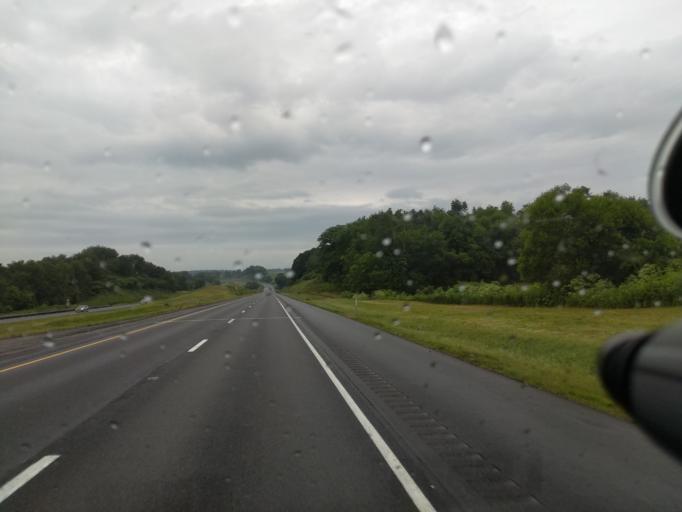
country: US
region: Pennsylvania
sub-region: Northumberland County
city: Milton
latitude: 41.0345
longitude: -76.8073
